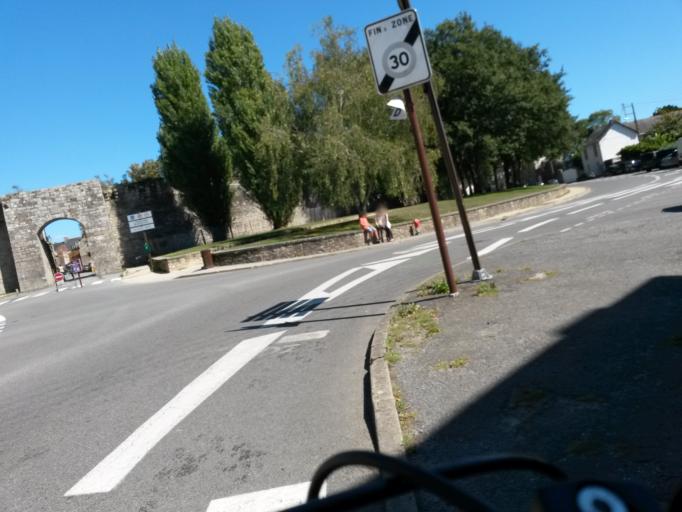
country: FR
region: Pays de la Loire
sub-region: Departement de la Loire-Atlantique
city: Guerande
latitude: 47.3270
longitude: -2.4331
